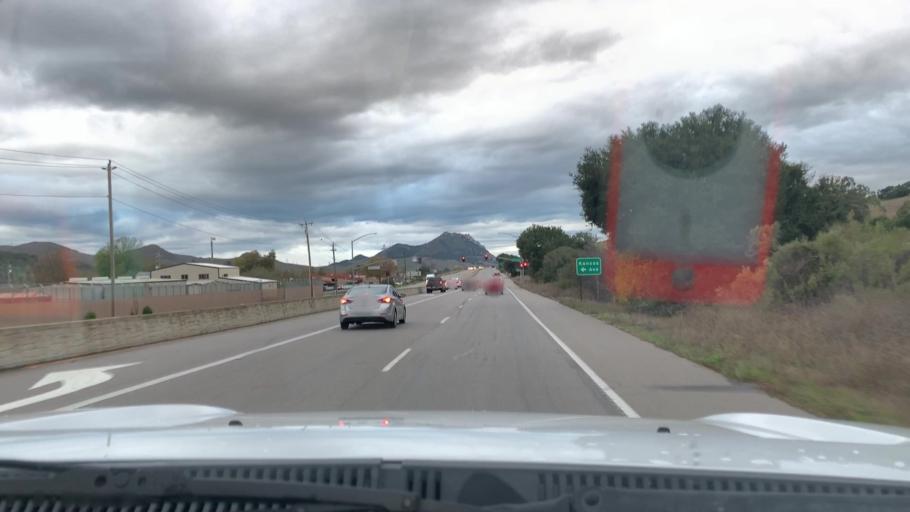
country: US
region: California
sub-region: San Luis Obispo County
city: San Luis Obispo
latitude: 35.3205
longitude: -120.7150
